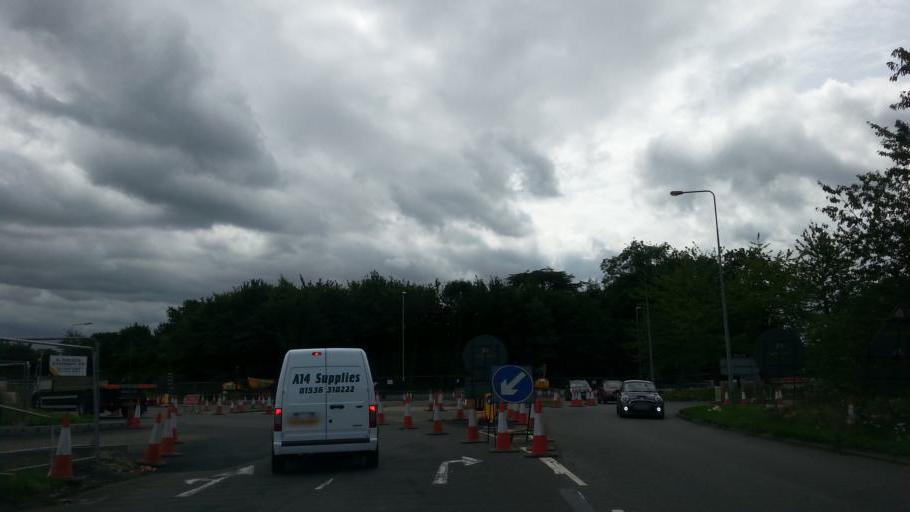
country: GB
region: England
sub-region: Northamptonshire
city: Northampton
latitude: 52.2897
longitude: -0.8372
